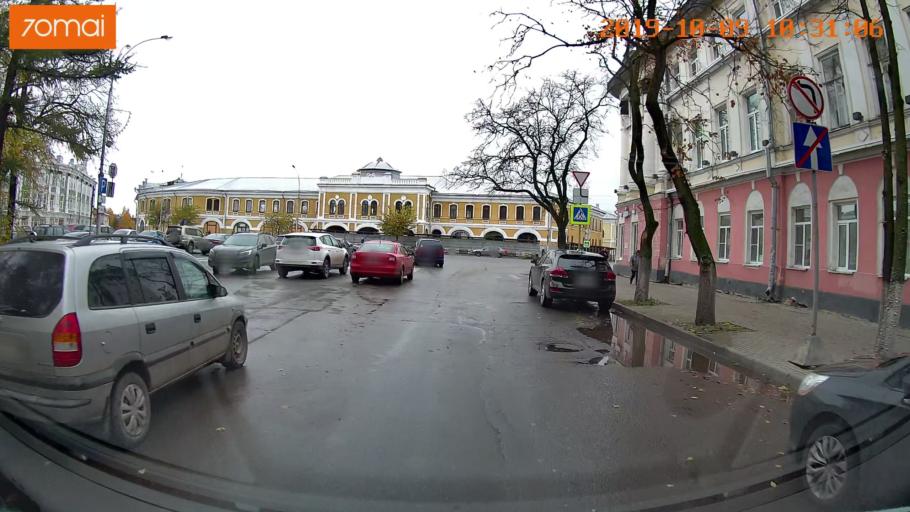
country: RU
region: Vologda
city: Vologda
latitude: 59.2209
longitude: 39.8933
